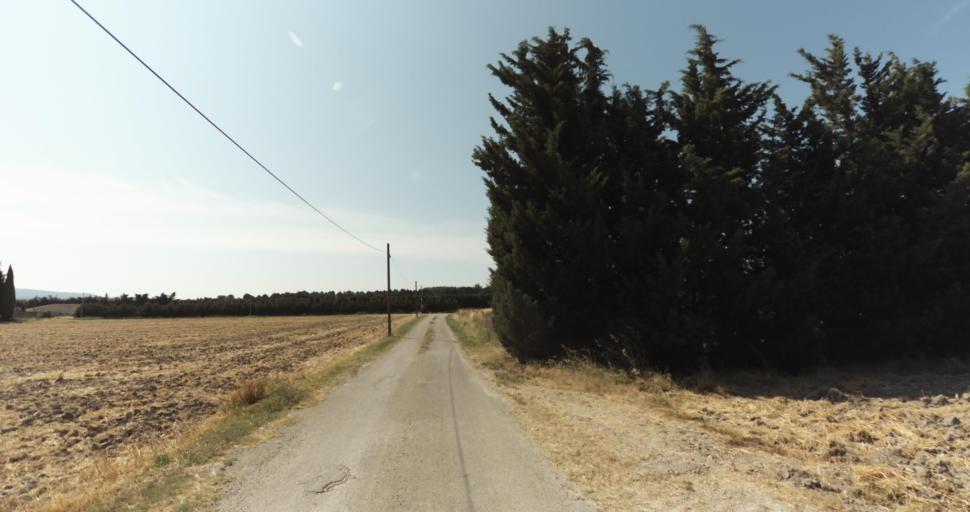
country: FR
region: Provence-Alpes-Cote d'Azur
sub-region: Departement du Vaucluse
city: Monteux
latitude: 44.0072
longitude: 4.9969
